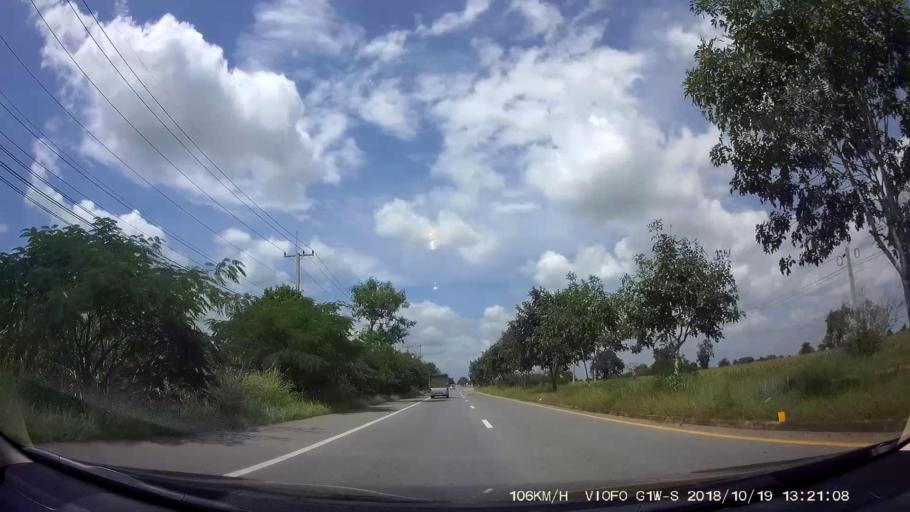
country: TH
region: Chaiyaphum
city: Chatturat
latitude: 15.4569
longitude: 101.8268
